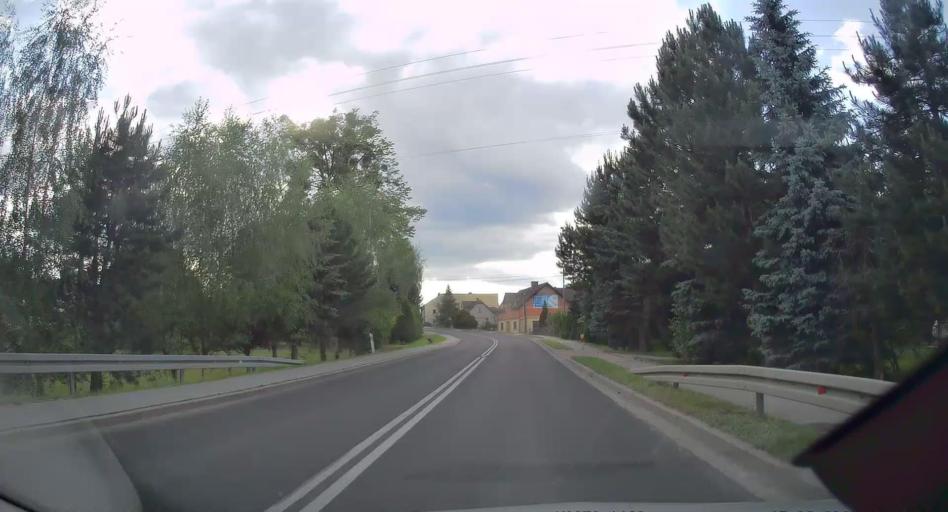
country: PL
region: Lesser Poland Voivodeship
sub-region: Powiat oswiecimski
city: Bulowice
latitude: 49.8763
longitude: 19.2857
